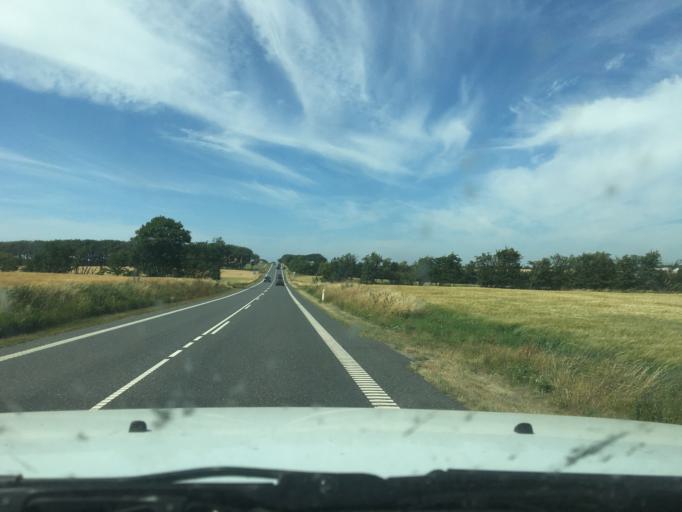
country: DK
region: Central Jutland
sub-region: Viborg Kommune
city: Viborg
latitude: 56.5825
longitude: 9.3721
